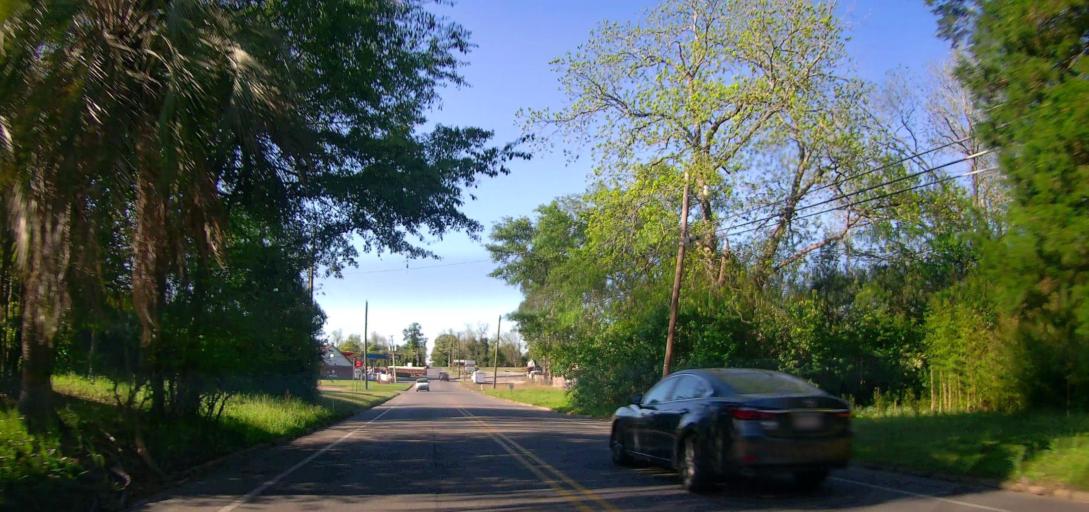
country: US
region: Georgia
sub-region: Ben Hill County
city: Fitzgerald
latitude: 31.7164
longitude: -83.2650
